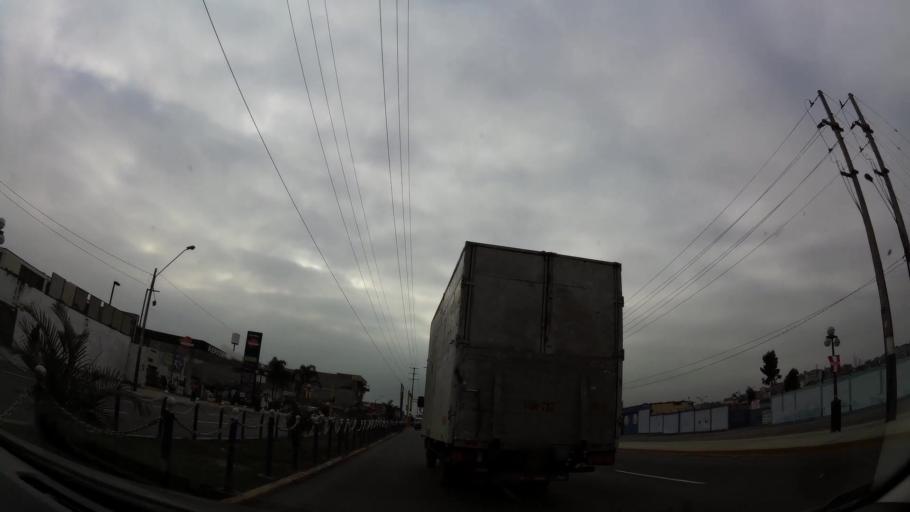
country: PE
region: Lima
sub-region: Lima
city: Surco
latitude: -12.1944
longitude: -77.0021
